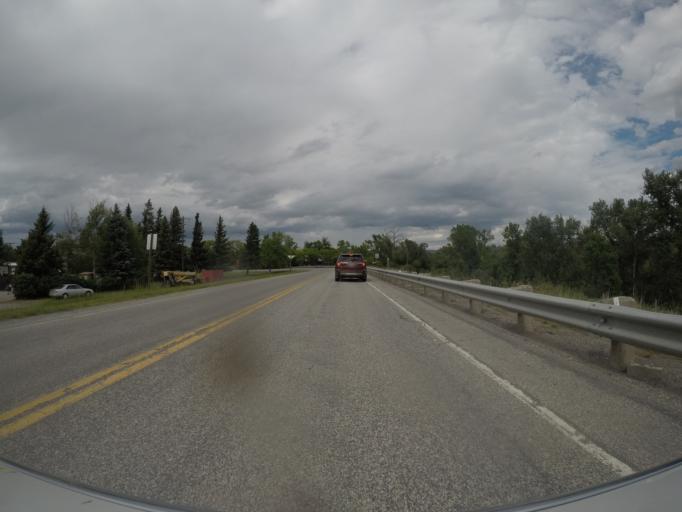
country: US
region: Montana
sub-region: Sweet Grass County
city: Big Timber
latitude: 45.8272
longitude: -109.9476
